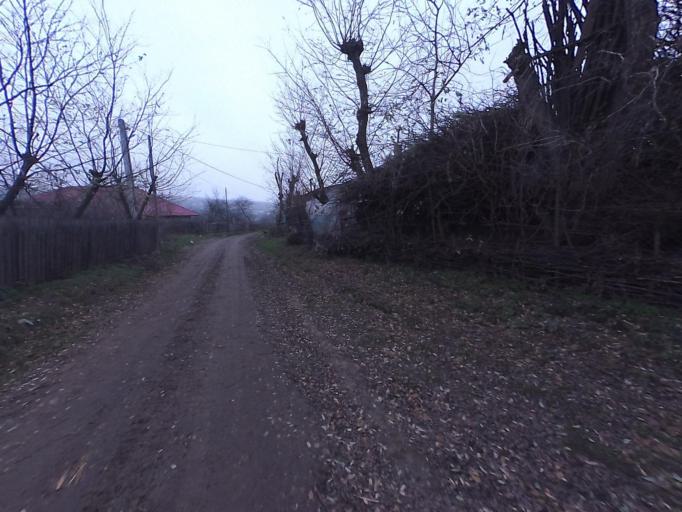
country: RO
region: Galati
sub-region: Comuna Balabanesti
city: Balabanesti
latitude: 46.1438
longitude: 27.7437
